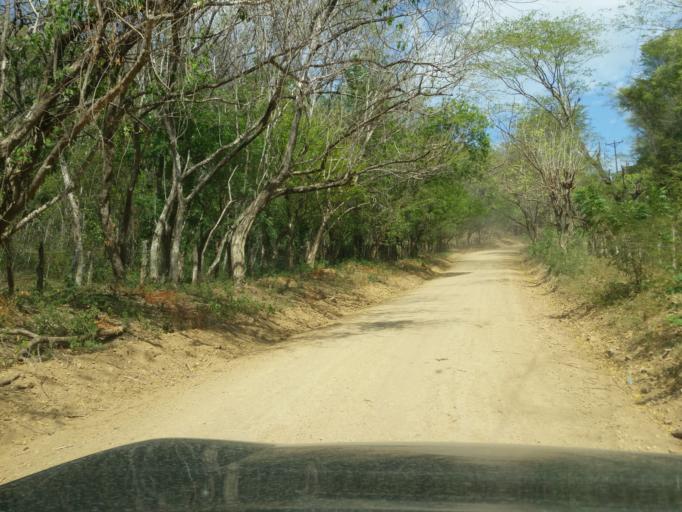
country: NI
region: Rivas
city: San Juan del Sur
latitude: 11.1446
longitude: -85.7911
